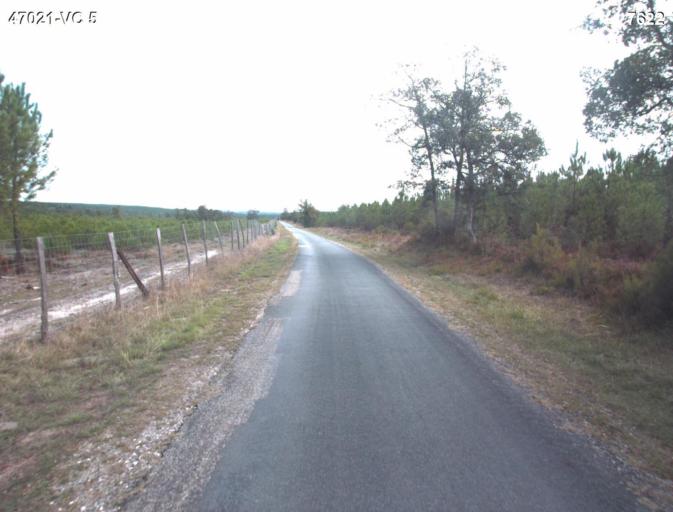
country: FR
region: Aquitaine
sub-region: Departement du Lot-et-Garonne
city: Barbaste
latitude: 44.1522
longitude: 0.2065
